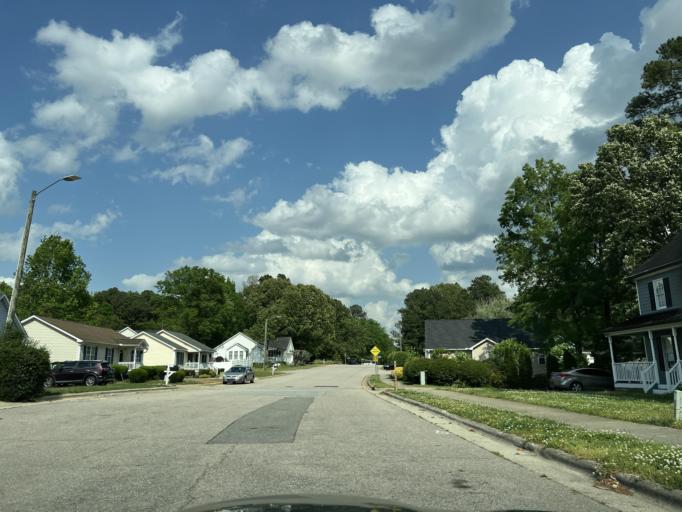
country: US
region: North Carolina
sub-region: Wake County
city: Rolesville
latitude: 35.8785
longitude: -78.5614
